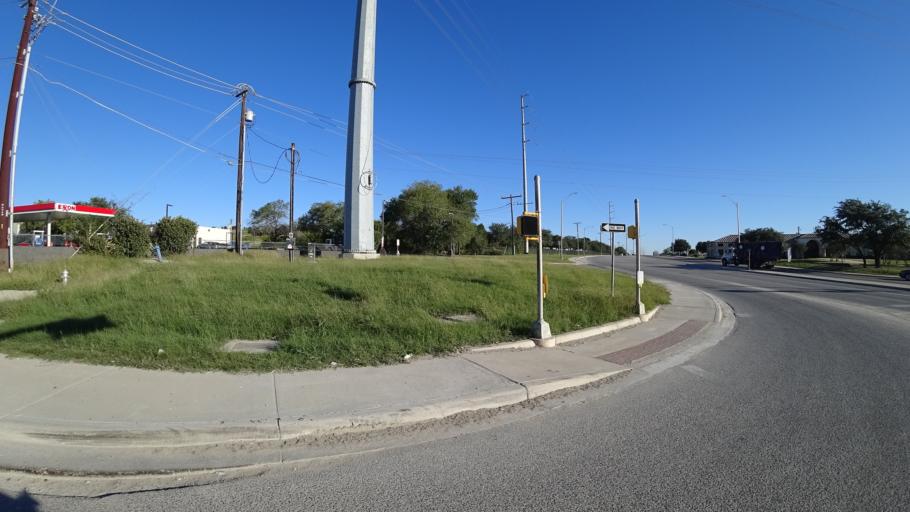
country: US
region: Texas
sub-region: Travis County
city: Manor
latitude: 30.3312
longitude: -97.6235
